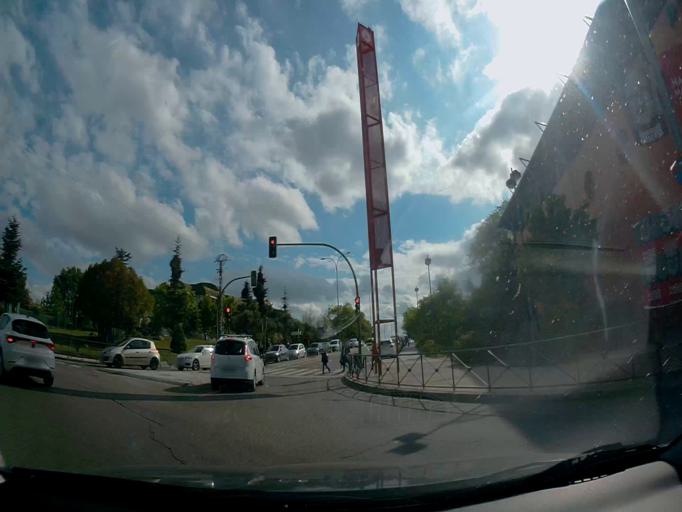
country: ES
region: Madrid
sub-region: Provincia de Madrid
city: Alcorcon
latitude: 40.3418
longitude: -3.8420
